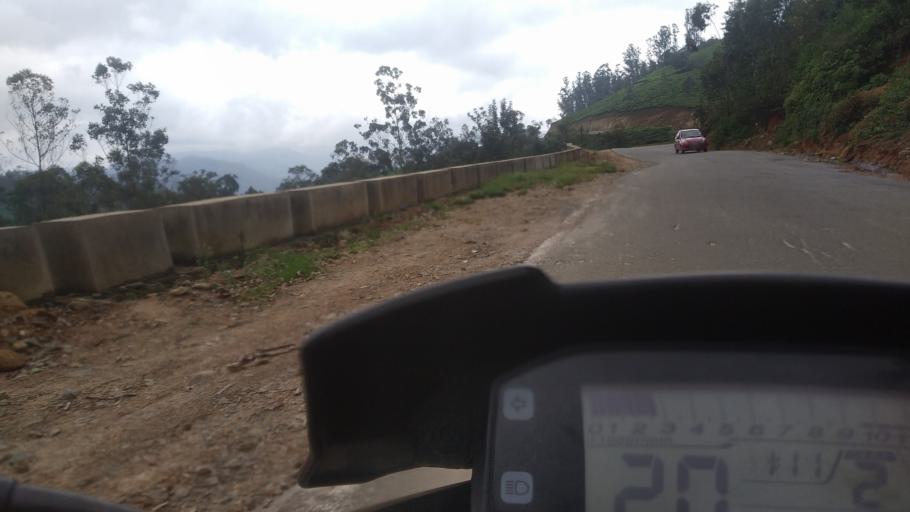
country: IN
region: Kerala
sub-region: Idukki
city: Munnar
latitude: 10.0823
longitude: 77.0746
